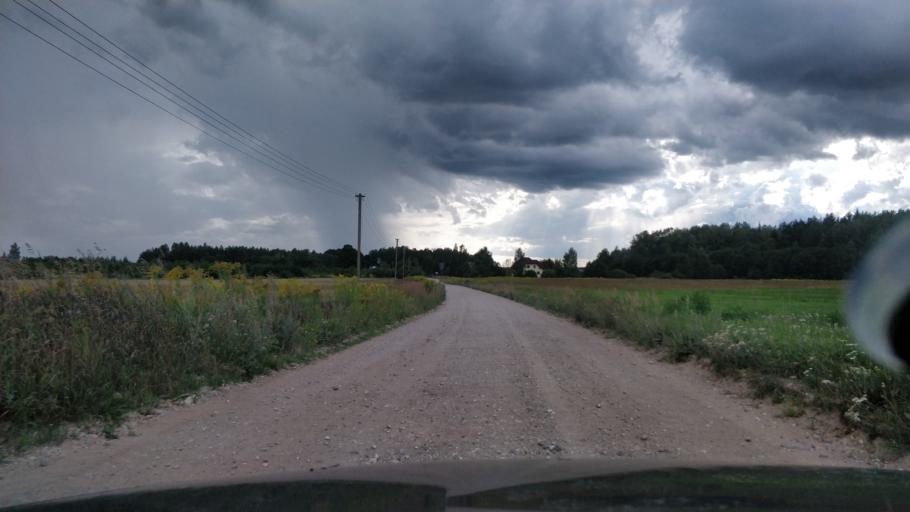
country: LV
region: Ogre
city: Ogre
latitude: 56.7960
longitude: 24.6570
